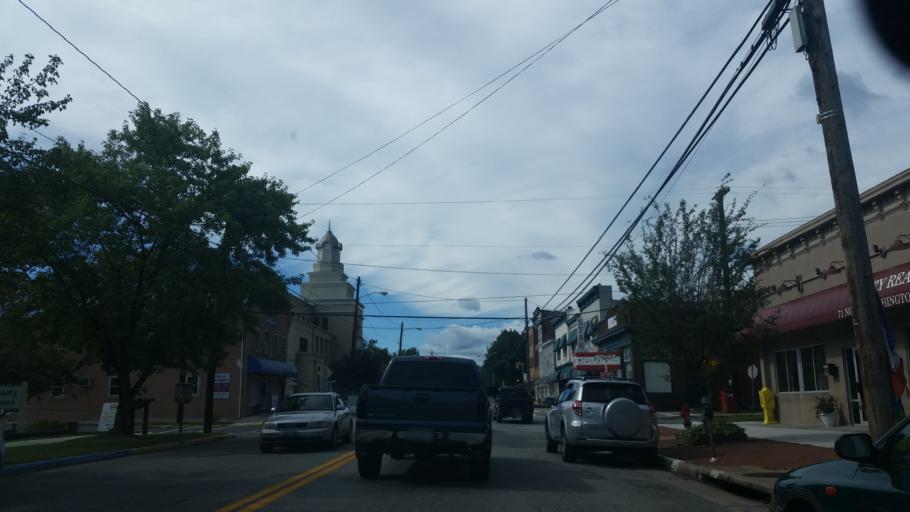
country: US
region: West Virginia
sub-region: Morgan County
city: Berkeley Springs
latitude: 39.6281
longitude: -78.2270
